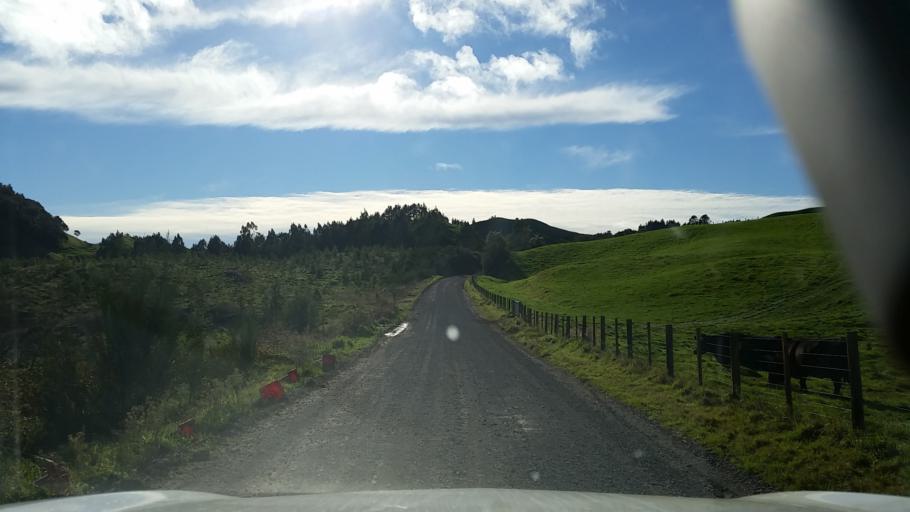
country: NZ
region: Bay of Plenty
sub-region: Rotorua District
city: Rotorua
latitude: -38.3600
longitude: 176.2114
